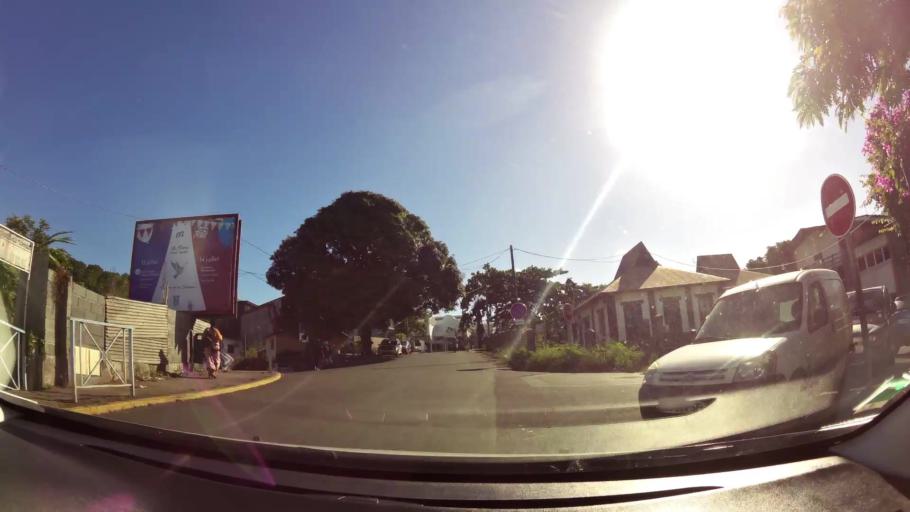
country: YT
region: Mamoudzou
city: Mamoudzou
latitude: -12.7777
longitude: 45.2292
